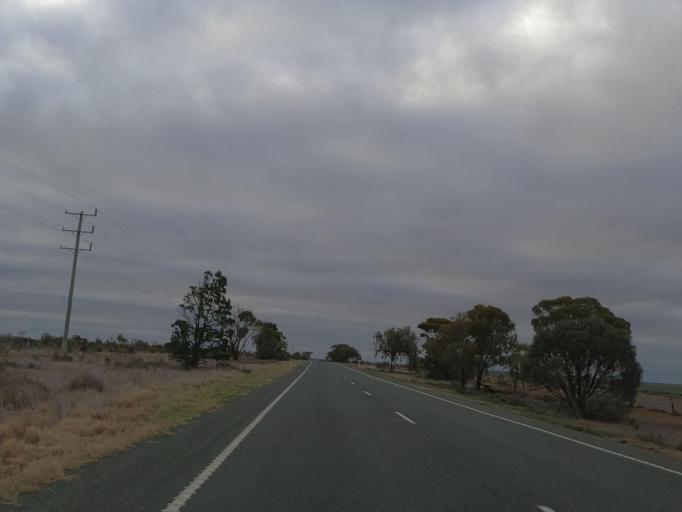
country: AU
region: Victoria
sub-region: Swan Hill
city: Swan Hill
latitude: -35.5717
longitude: 143.7863
